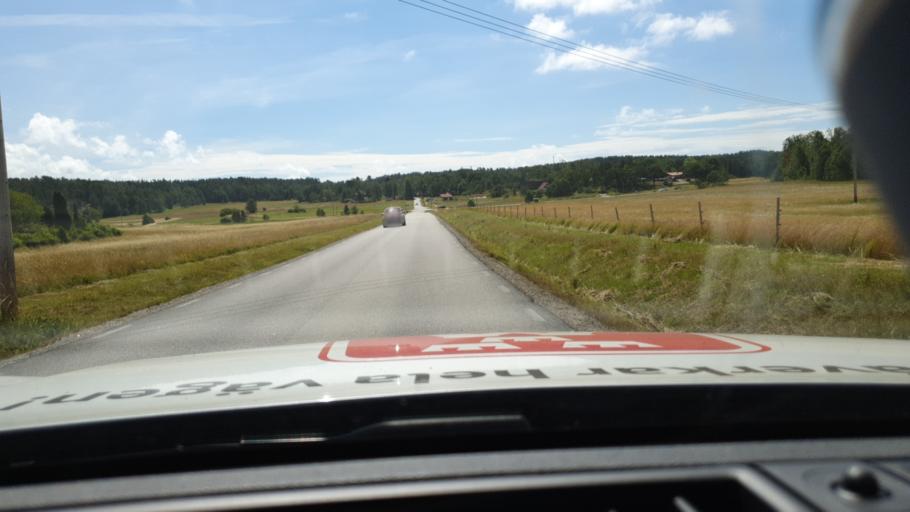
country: SE
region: Stockholm
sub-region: Haninge Kommun
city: Jordbro
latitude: 59.0110
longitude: 18.1310
